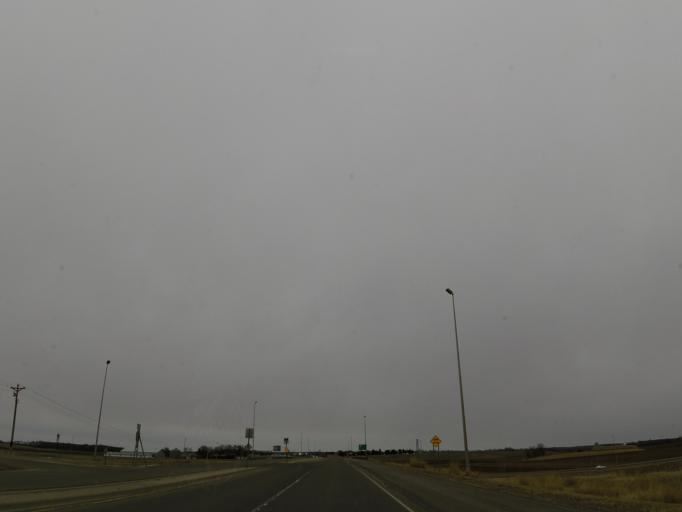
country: US
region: Minnesota
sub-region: Le Sueur County
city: Le Sueur
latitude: 44.5430
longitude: -93.8525
